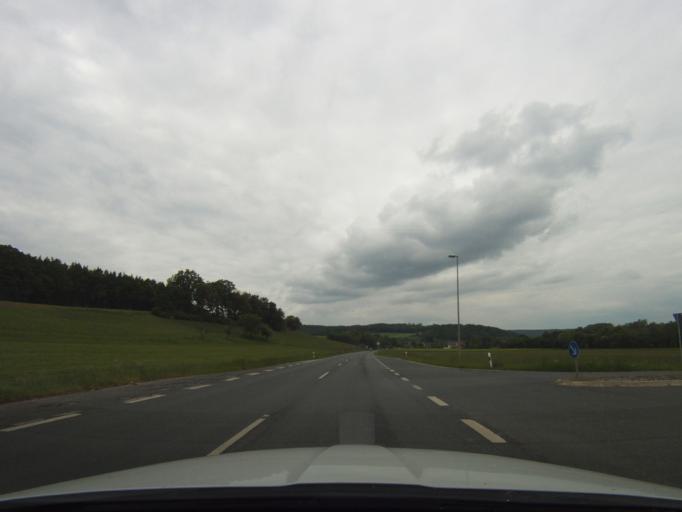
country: DE
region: Bavaria
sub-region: Upper Franconia
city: Altenkunstadt
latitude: 50.1133
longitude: 11.2322
